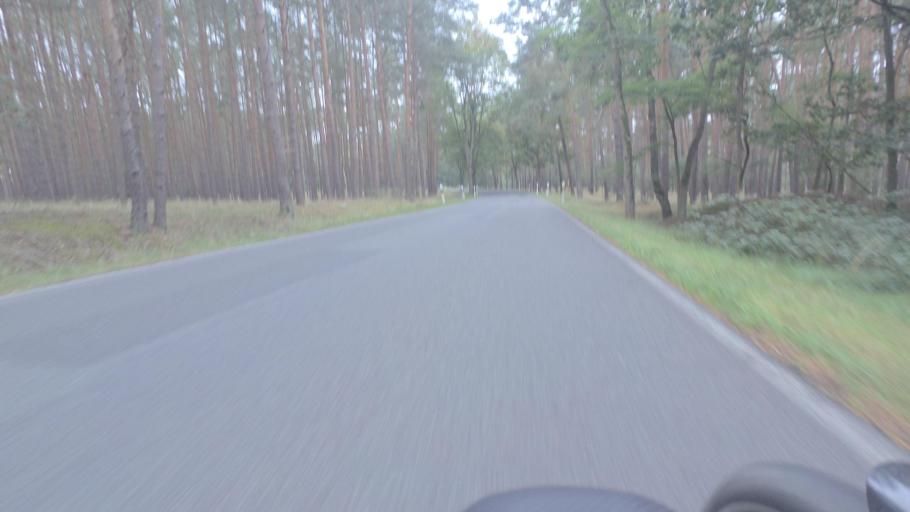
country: DE
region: Brandenburg
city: Luckenwalde
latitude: 52.1308
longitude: 13.1905
